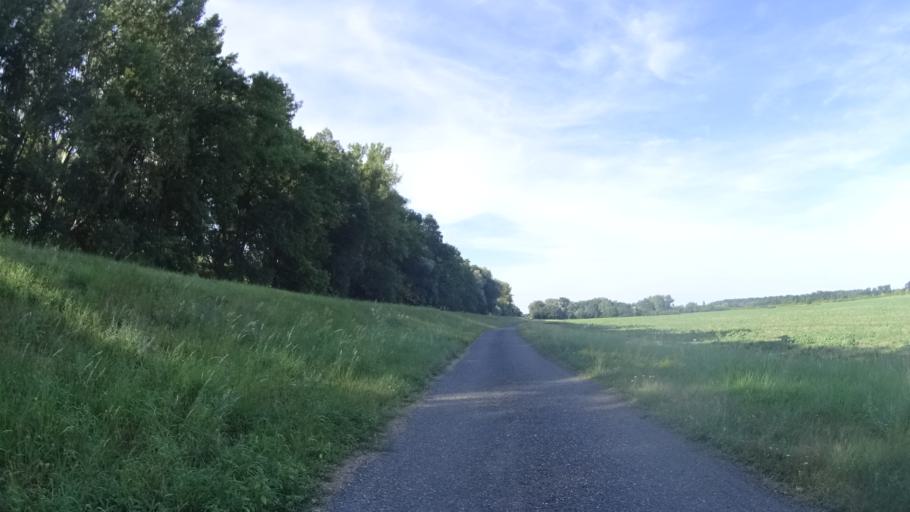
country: AT
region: Lower Austria
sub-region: Politischer Bezirk Ganserndorf
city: Drosing
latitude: 48.5390
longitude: 16.9580
